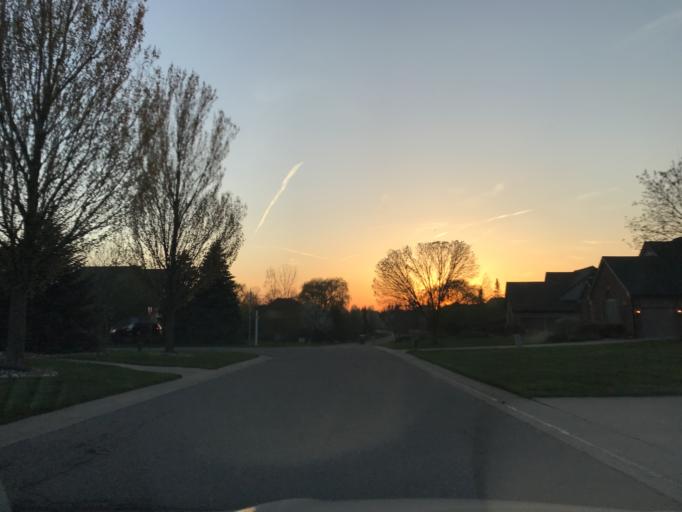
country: US
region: Michigan
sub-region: Oakland County
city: South Lyon
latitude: 42.4584
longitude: -83.5855
